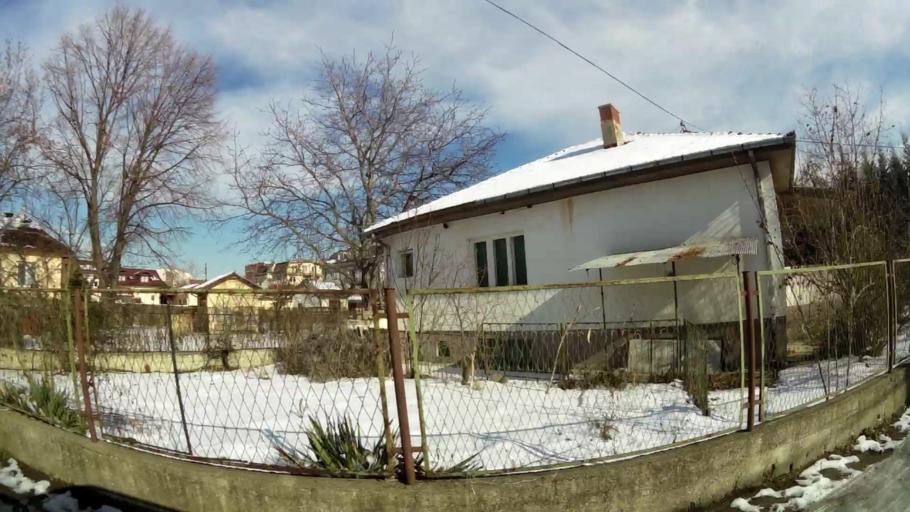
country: MK
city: Krushopek
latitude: 42.0002
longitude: 21.3693
